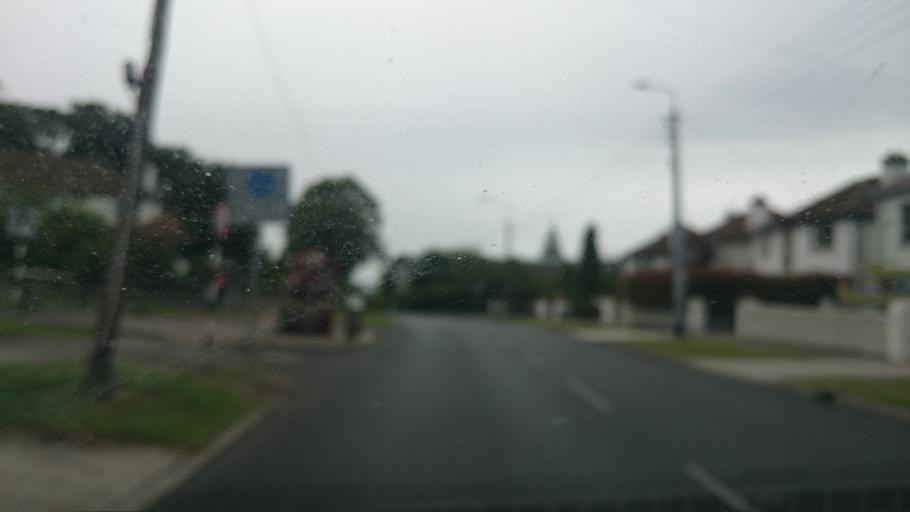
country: IE
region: Leinster
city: Mount Merrion
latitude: 53.2936
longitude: -6.2106
